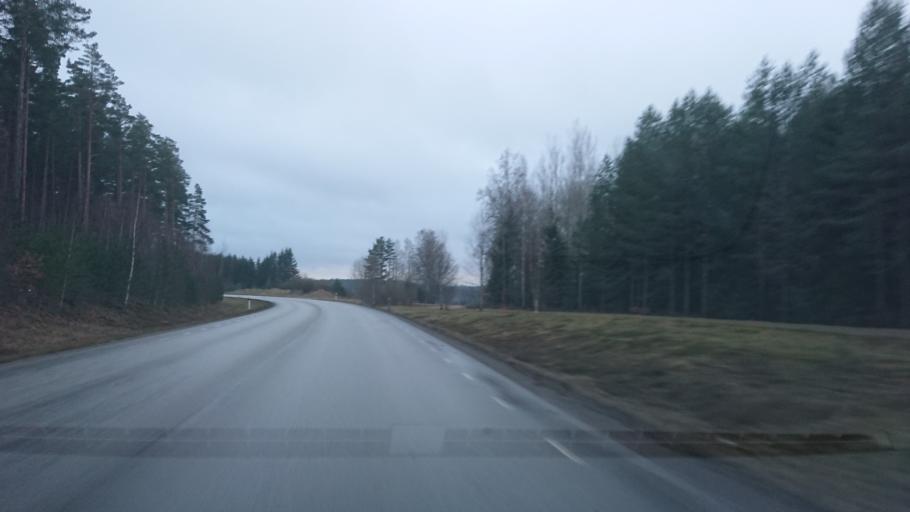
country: SE
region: Uppsala
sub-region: Osthammars Kommun
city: Bjorklinge
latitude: 60.0142
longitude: 17.5866
